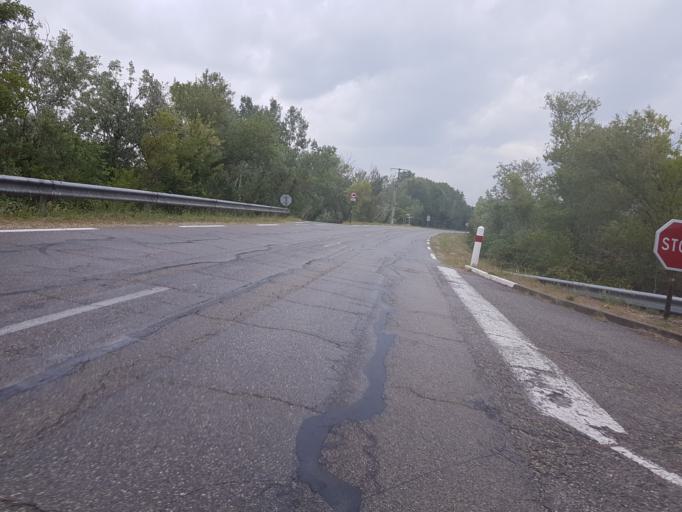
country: FR
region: Languedoc-Roussillon
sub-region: Departement du Gard
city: Villeneuve-les-Avignon
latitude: 43.9758
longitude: 4.8206
